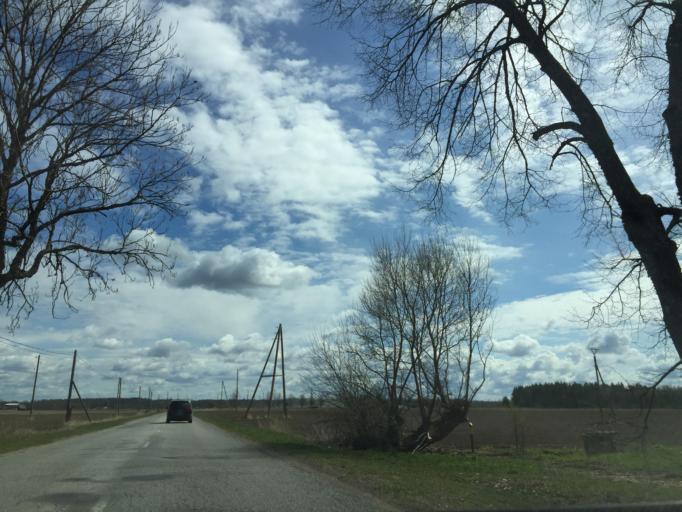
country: LV
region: Salacgrivas
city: Salacgriva
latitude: 57.7463
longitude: 24.3839
